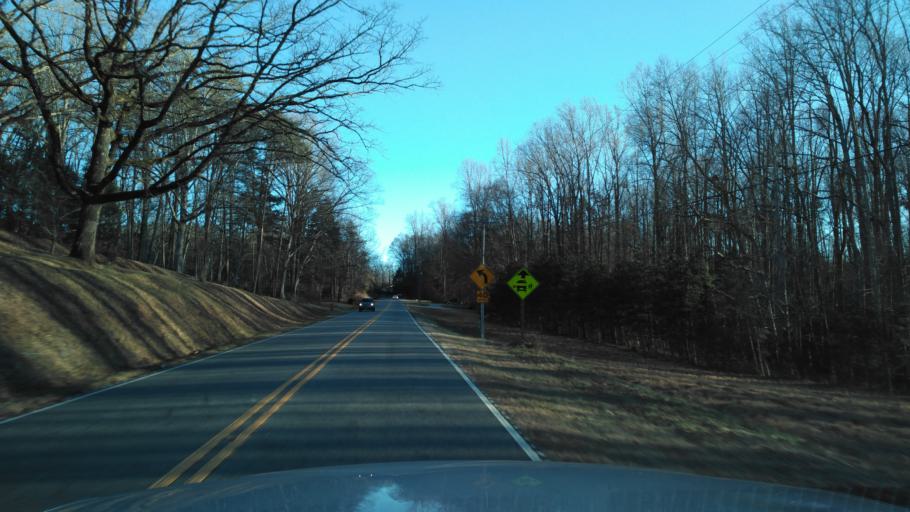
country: US
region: North Carolina
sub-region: Polk County
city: Columbus
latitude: 35.2596
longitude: -82.1048
